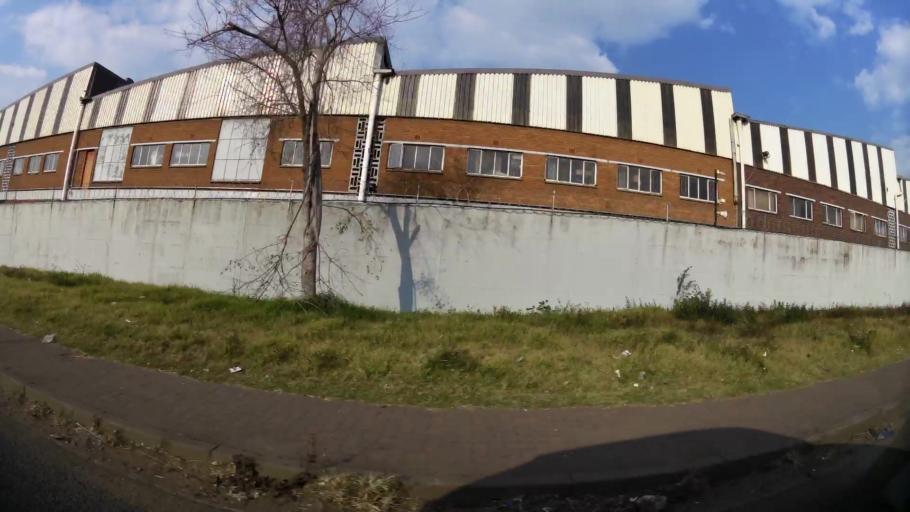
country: ZA
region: Gauteng
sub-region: City of Johannesburg Metropolitan Municipality
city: Modderfontein
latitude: -26.1163
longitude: 28.2084
